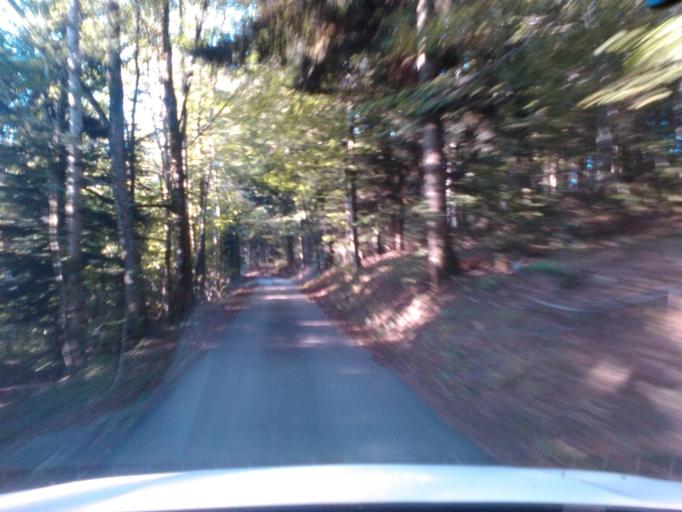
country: FR
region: Lorraine
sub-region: Departement des Vosges
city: Senones
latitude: 48.3423
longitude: 7.0545
